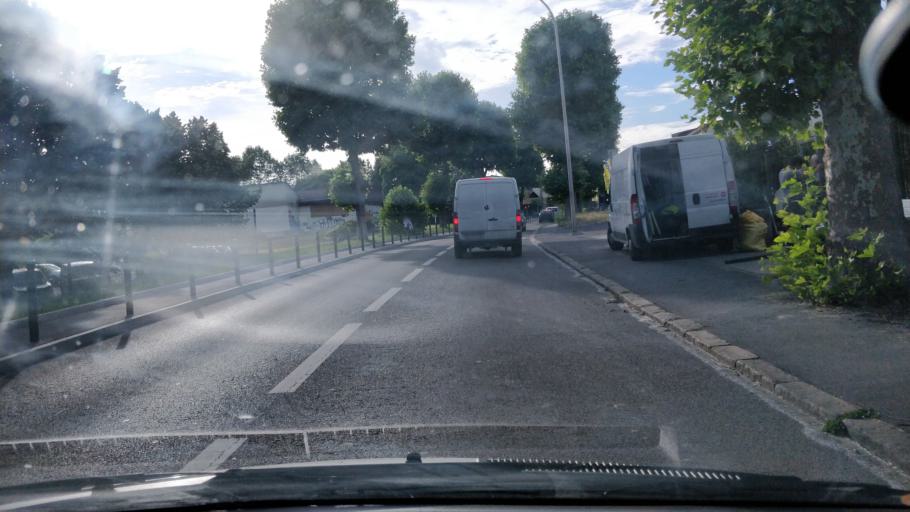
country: FR
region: Ile-de-France
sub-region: Departement de Seine-Saint-Denis
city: Neuilly-sur-Marne
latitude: 48.8673
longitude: 2.5586
